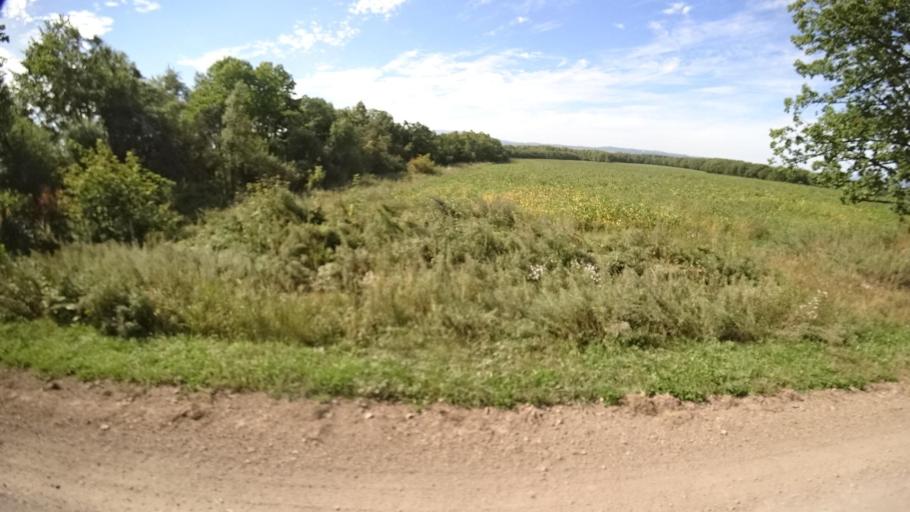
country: RU
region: Primorskiy
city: Yakovlevka
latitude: 44.4160
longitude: 133.5706
